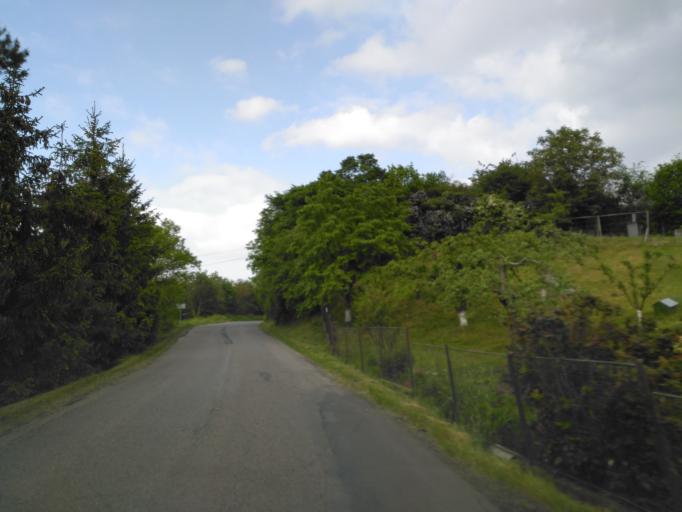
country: CZ
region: Plzensky
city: Zbiroh
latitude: 49.8631
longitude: 13.7831
